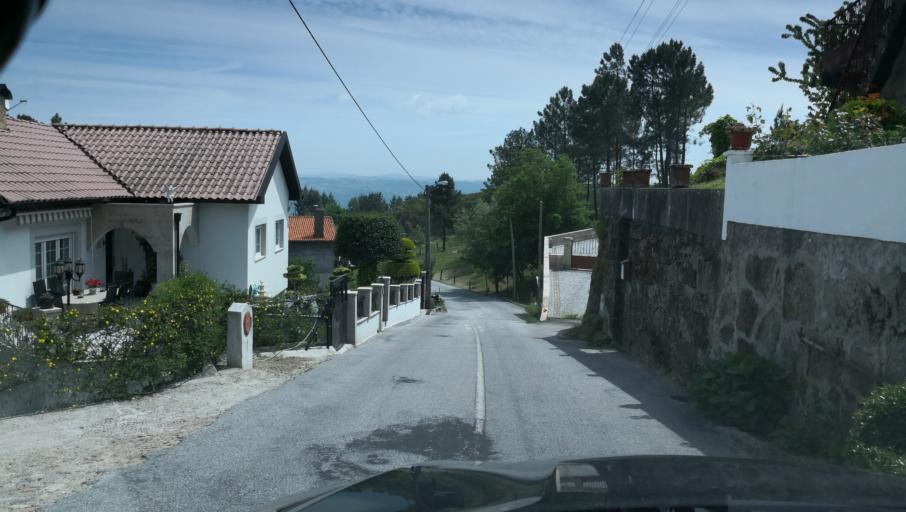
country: PT
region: Vila Real
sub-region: Vila Real
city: Vila Real
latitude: 41.3132
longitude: -7.7857
